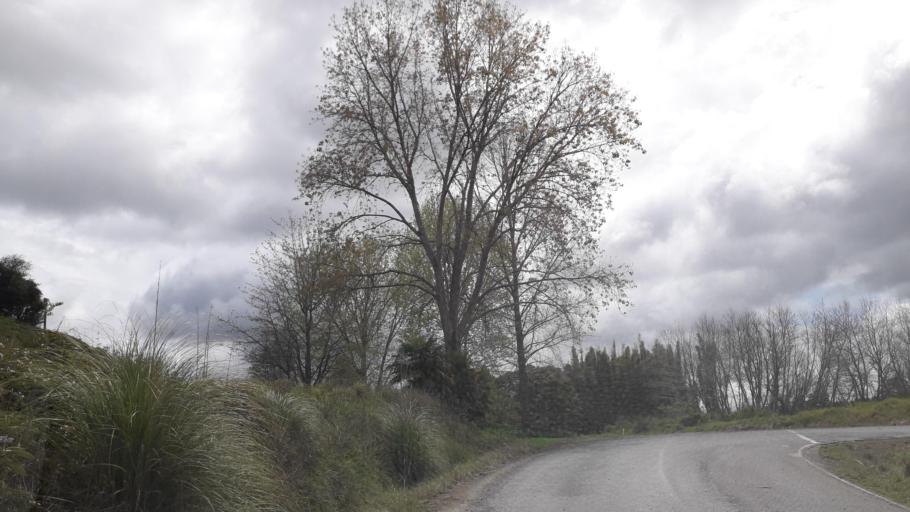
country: NZ
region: Northland
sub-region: Far North District
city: Kaitaia
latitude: -35.1633
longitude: 173.3446
